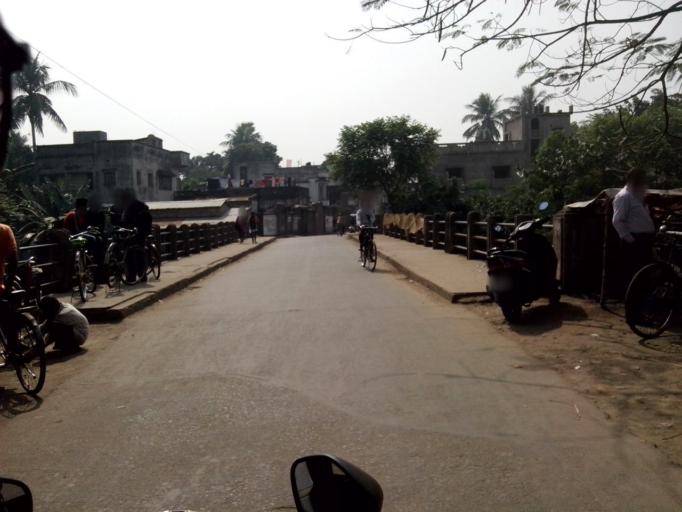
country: IN
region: West Bengal
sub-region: Barddhaman
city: Barddhaman
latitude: 23.2331
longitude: 87.8723
